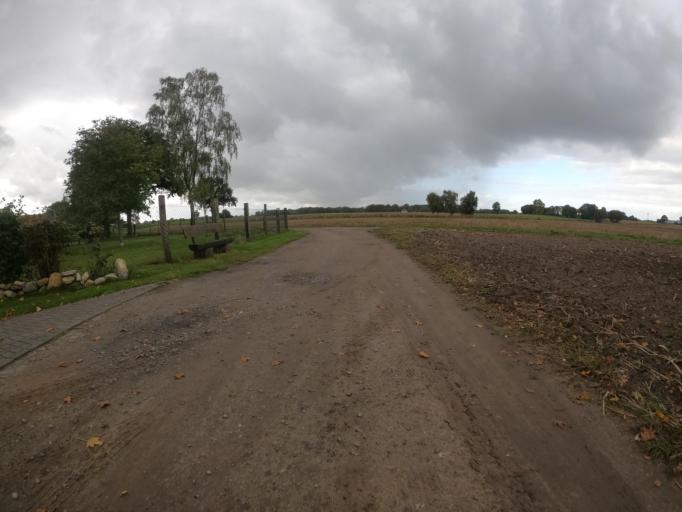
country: DE
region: North Rhine-Westphalia
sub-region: Regierungsbezirk Dusseldorf
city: Schermbeck
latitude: 51.7242
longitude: 6.8732
